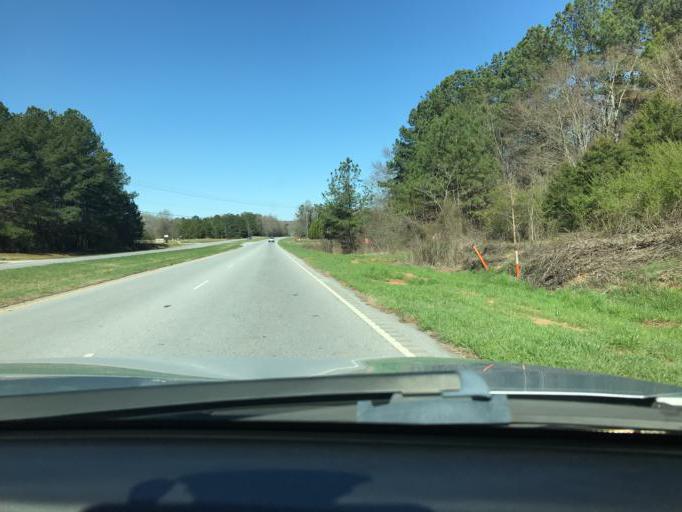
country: US
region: South Carolina
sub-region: Laurens County
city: Watts Mills
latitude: 34.4825
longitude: -81.9514
